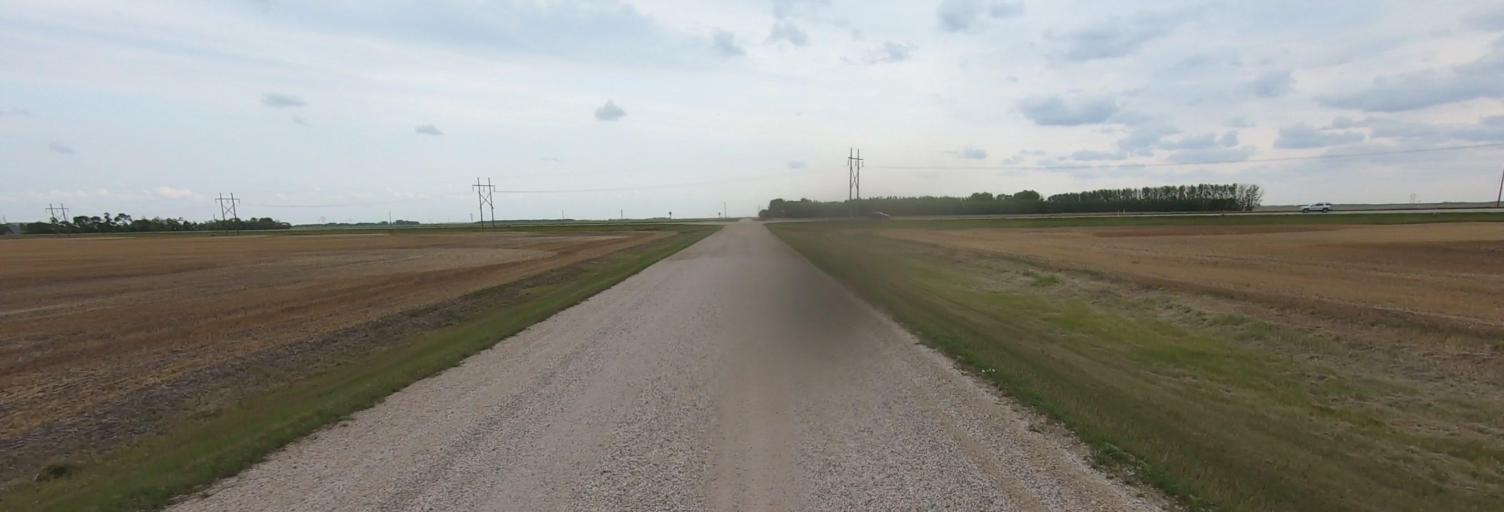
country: CA
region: Manitoba
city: Headingley
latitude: 49.7242
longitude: -97.3745
